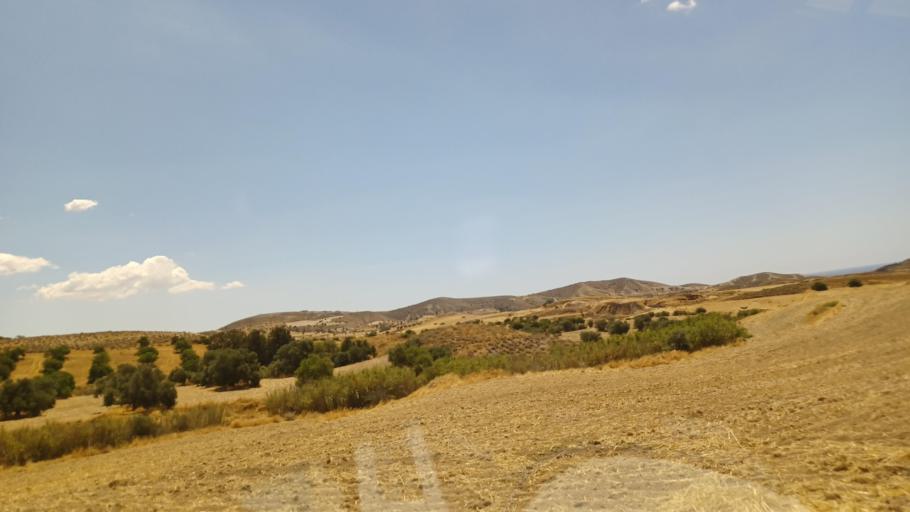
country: CY
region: Larnaka
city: Troulloi
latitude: 35.0344
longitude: 33.6332
